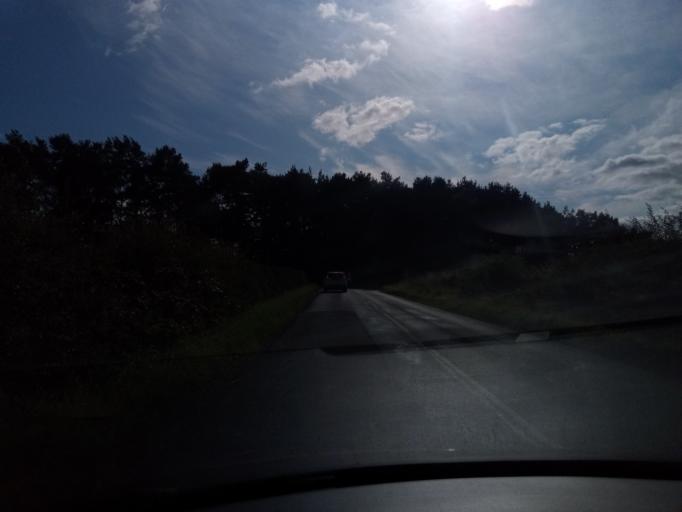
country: GB
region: Scotland
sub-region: The Scottish Borders
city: Allanton
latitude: 55.7562
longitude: -2.1293
